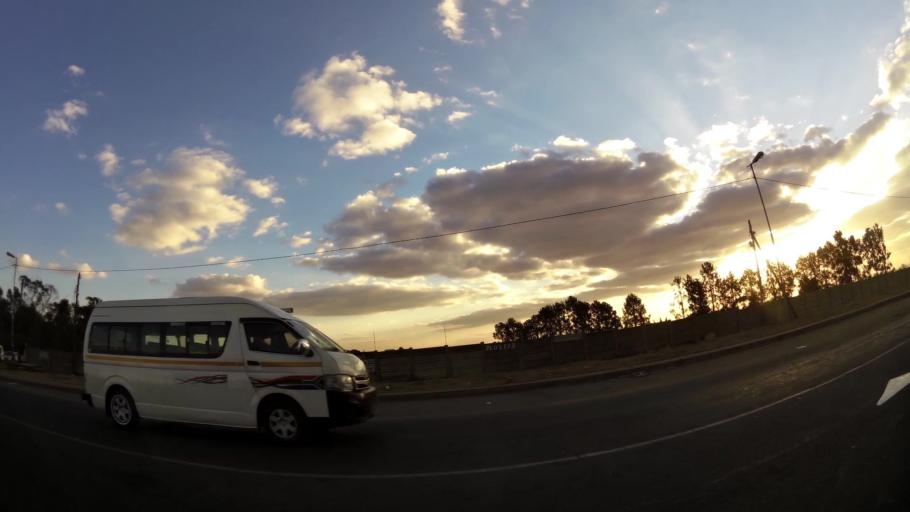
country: ZA
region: Gauteng
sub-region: City of Johannesburg Metropolitan Municipality
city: Midrand
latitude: -25.9889
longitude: 28.1530
